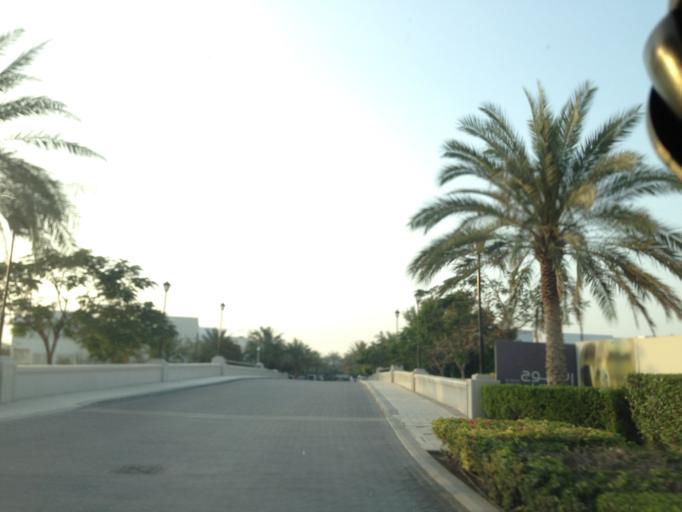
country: OM
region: Muhafazat Masqat
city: As Sib al Jadidah
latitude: 23.6231
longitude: 58.2740
